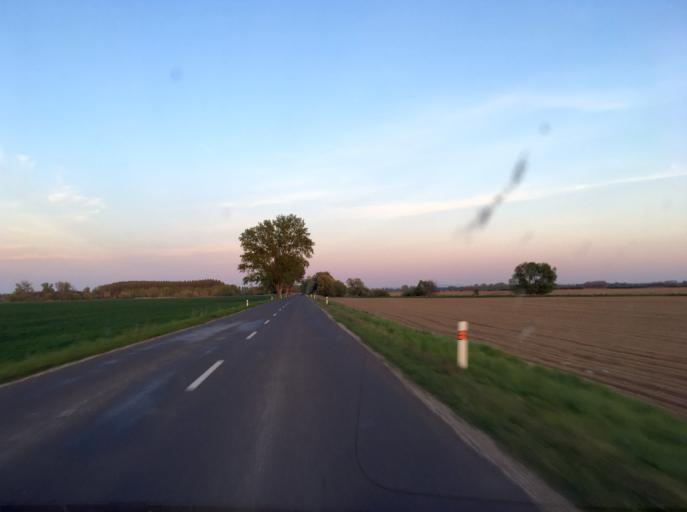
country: SK
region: Nitriansky
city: Kolarovo
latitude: 47.9200
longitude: 18.0392
